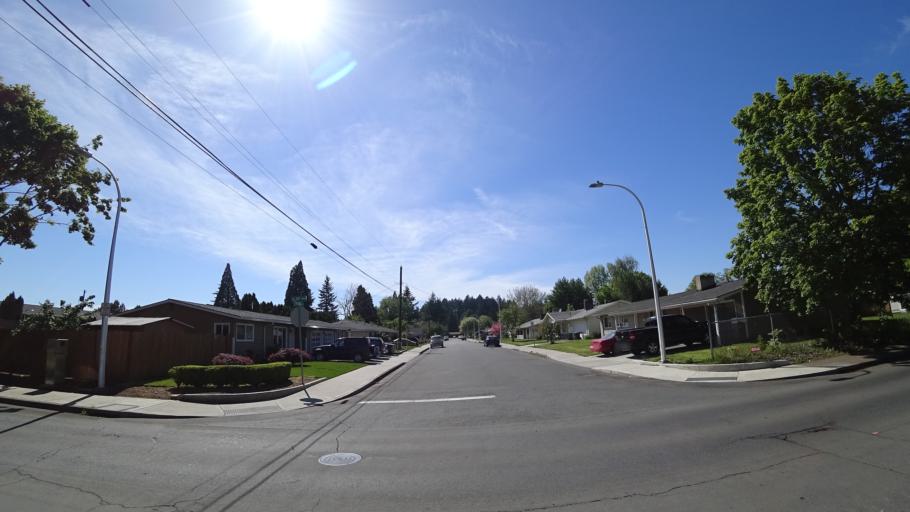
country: US
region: Oregon
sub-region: Washington County
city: Hillsboro
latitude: 45.5135
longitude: -122.9690
